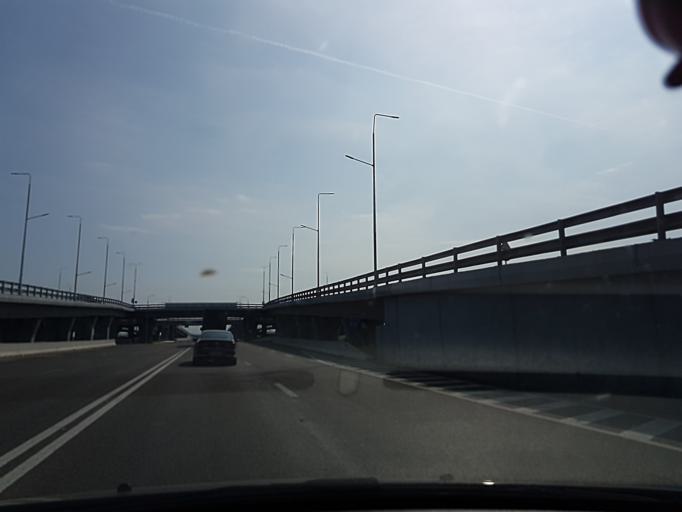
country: RO
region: Prahova
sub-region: Comuna Paulesti
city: Paulesti
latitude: 44.9784
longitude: 25.9939
